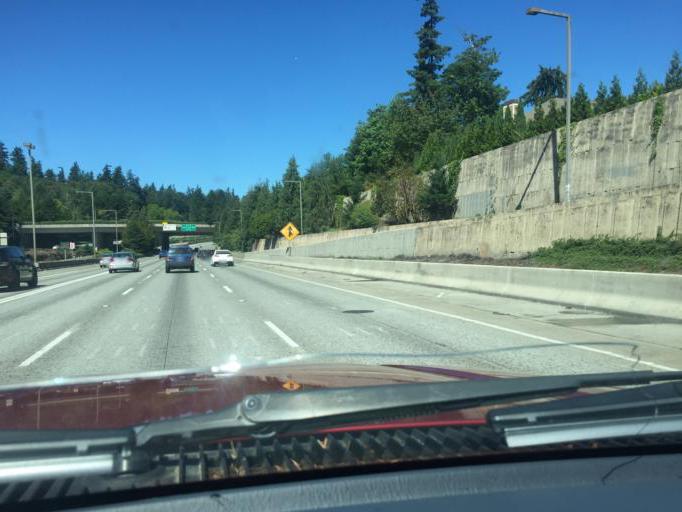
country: US
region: Washington
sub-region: King County
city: Mercer Island
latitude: 47.5785
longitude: -122.2089
